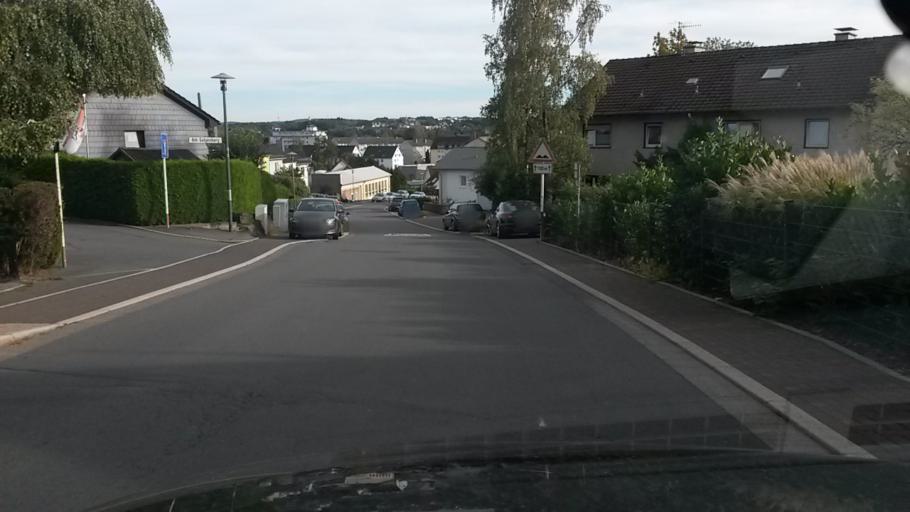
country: DE
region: North Rhine-Westphalia
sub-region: Regierungsbezirk Arnsberg
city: Luedenscheid
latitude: 51.2305
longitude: 7.6478
